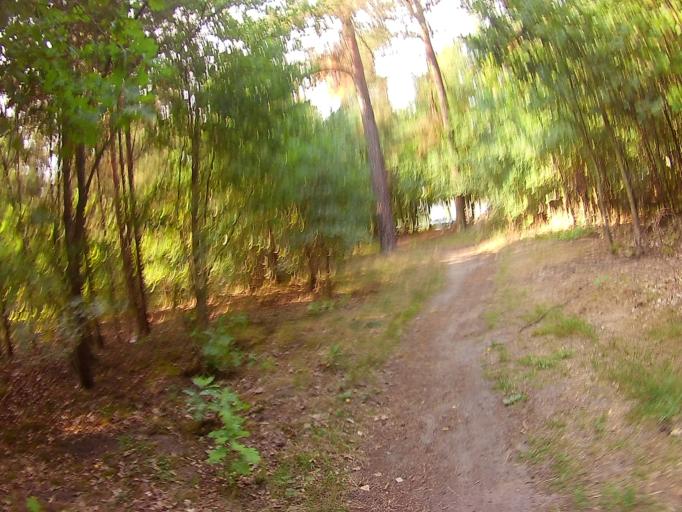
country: DE
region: Berlin
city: Grunau
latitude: 52.4227
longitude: 13.5717
